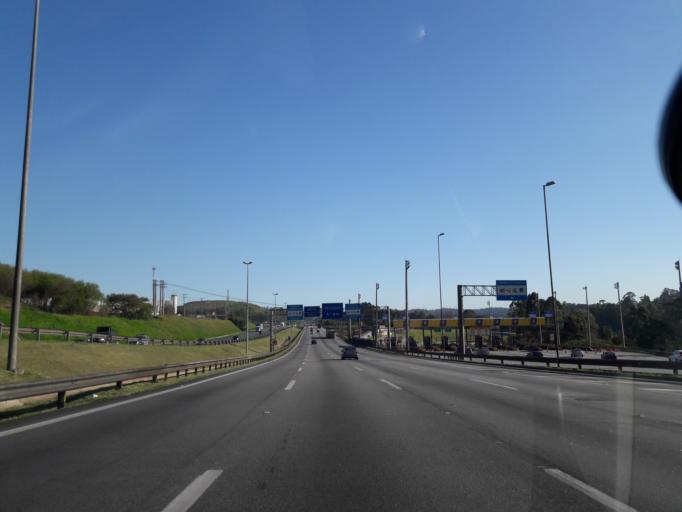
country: BR
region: Sao Paulo
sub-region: Taboao Da Serra
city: Taboao da Serra
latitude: -23.5872
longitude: -46.8090
